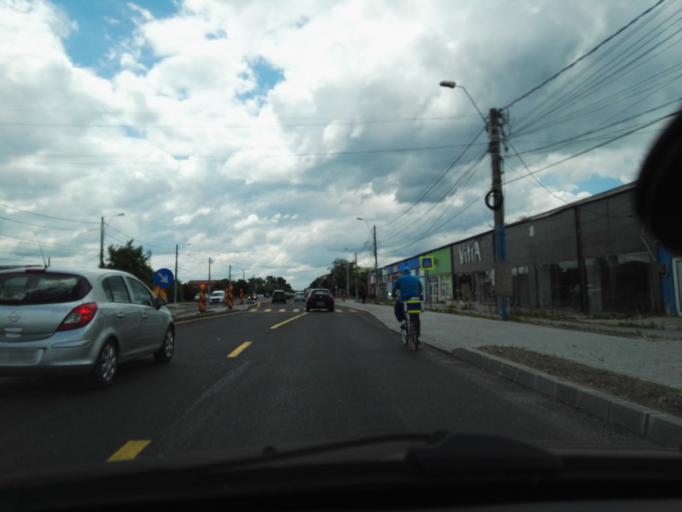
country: RO
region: Ilfov
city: Prim Decembrie
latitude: 44.2961
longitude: 26.0612
